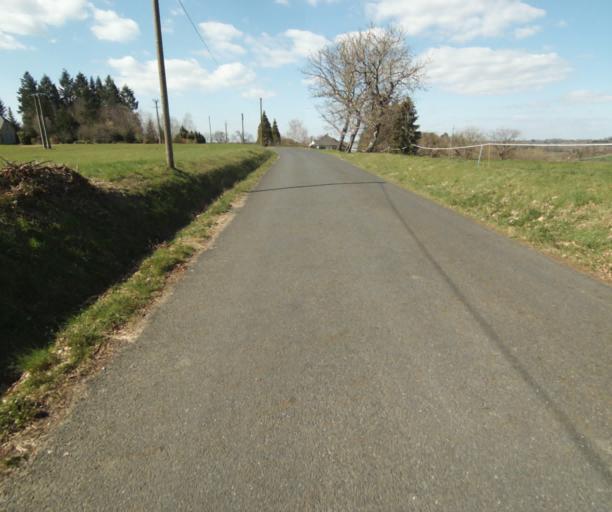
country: FR
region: Limousin
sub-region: Departement de la Correze
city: Saint-Mexant
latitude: 45.2928
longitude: 1.6512
